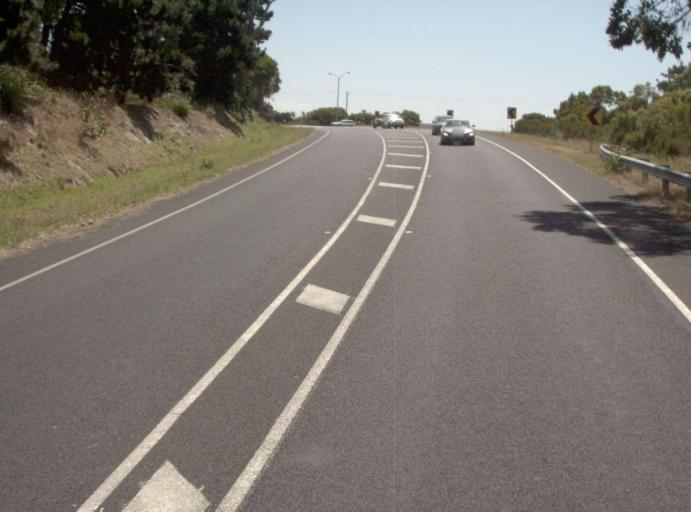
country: AU
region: Victoria
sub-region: Bass Coast
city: North Wonthaggi
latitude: -38.6850
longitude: 145.8772
